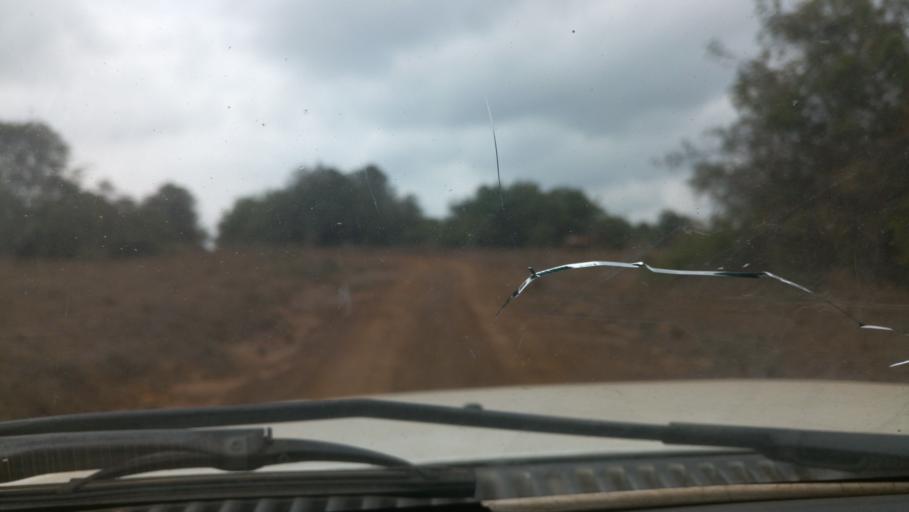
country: KE
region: Nairobi Area
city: Nairobi
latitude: -1.3582
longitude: 36.7775
